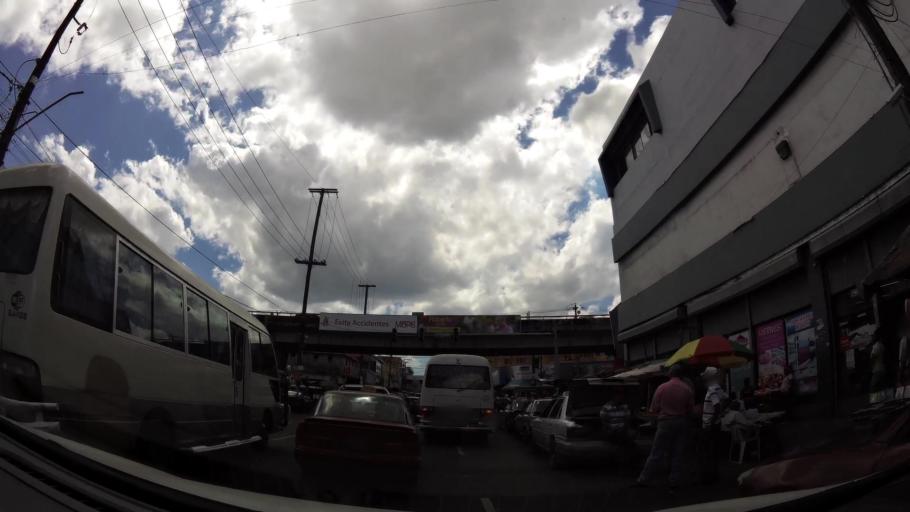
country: DO
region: Nacional
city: San Carlos
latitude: 18.4847
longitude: -69.8928
